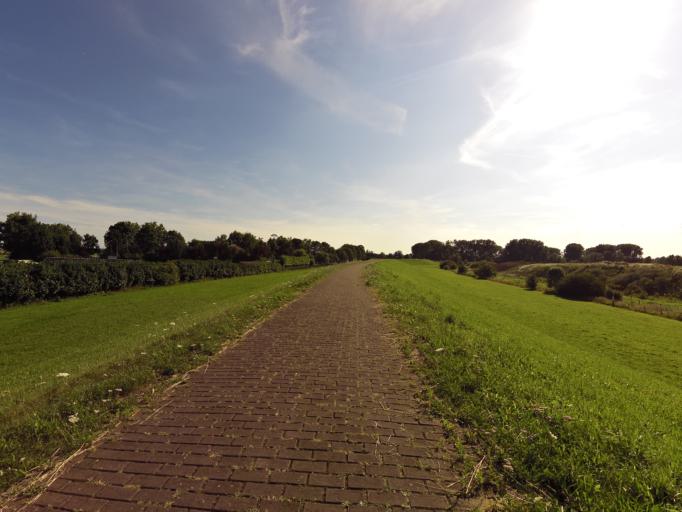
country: NL
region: Gelderland
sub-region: Gemeente Zevenaar
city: Zevenaar
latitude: 51.8683
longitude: 6.0272
